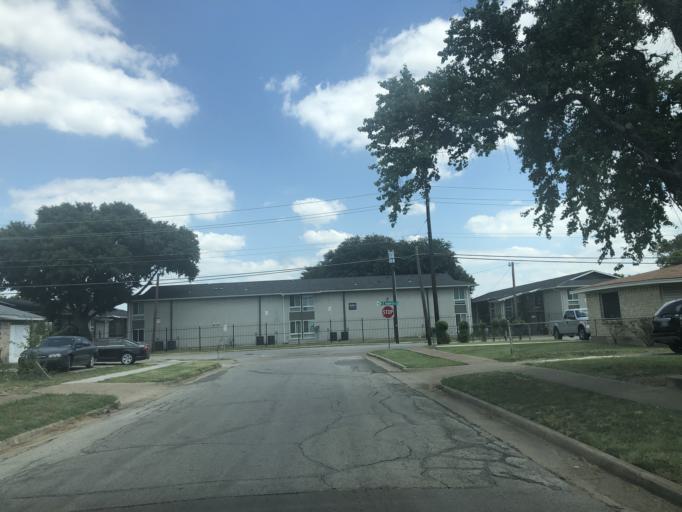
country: US
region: Texas
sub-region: Dallas County
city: Grand Prairie
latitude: 32.7346
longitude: -97.0363
